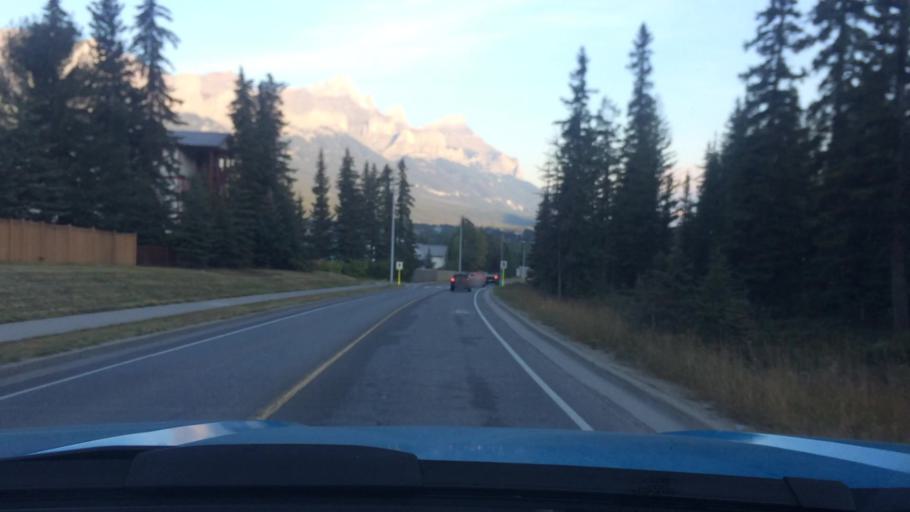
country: CA
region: Alberta
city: Canmore
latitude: 51.0882
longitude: -115.3355
